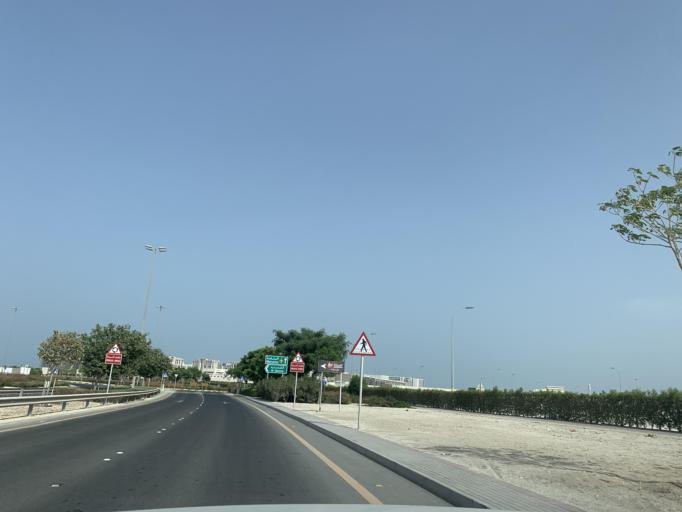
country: BH
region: Muharraq
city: Al Muharraq
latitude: 26.3087
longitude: 50.6335
